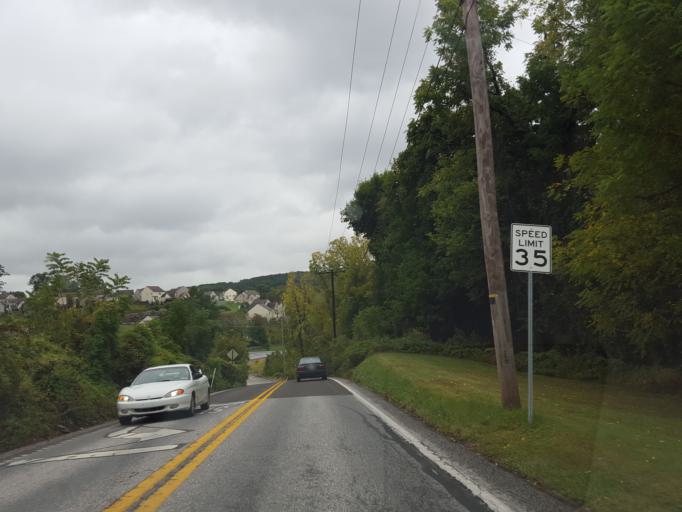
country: US
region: Pennsylvania
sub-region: York County
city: Yoe
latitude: 39.9365
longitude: -76.6541
